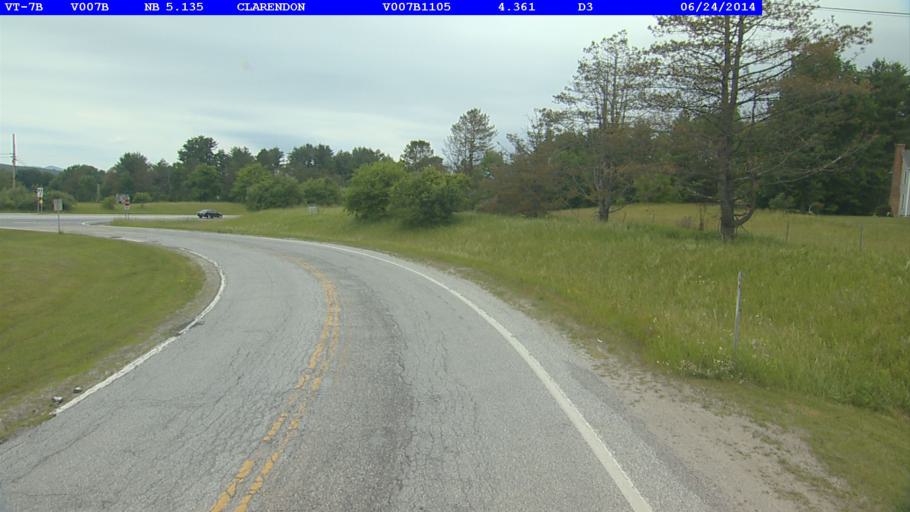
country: US
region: Vermont
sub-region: Rutland County
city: Rutland
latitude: 43.5602
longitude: -72.9634
